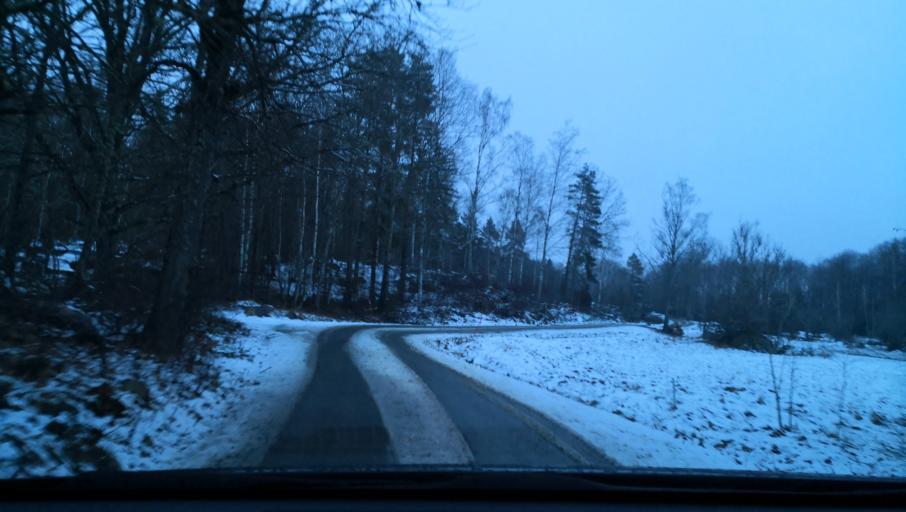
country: SE
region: Soedermanland
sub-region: Eskilstuna Kommun
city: Kvicksund
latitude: 59.3939
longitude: 16.2147
